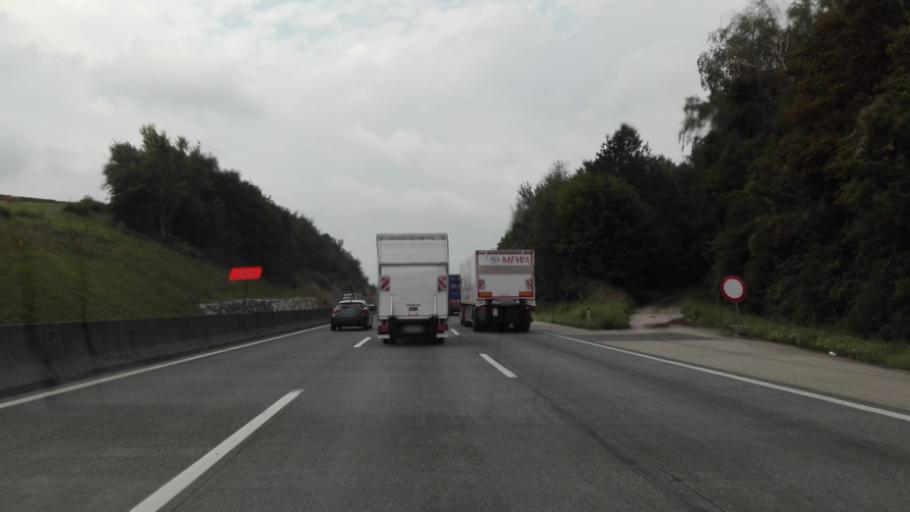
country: AT
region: Lower Austria
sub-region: Politischer Bezirk Melk
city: Erlauf
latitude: 48.1725
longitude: 15.1808
